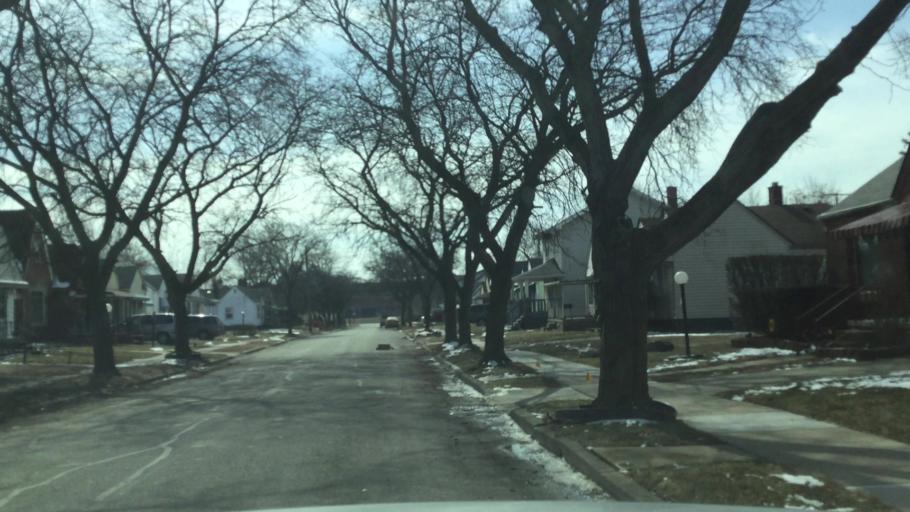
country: US
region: Michigan
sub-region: Wayne County
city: Dearborn
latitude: 42.3543
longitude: -83.1498
